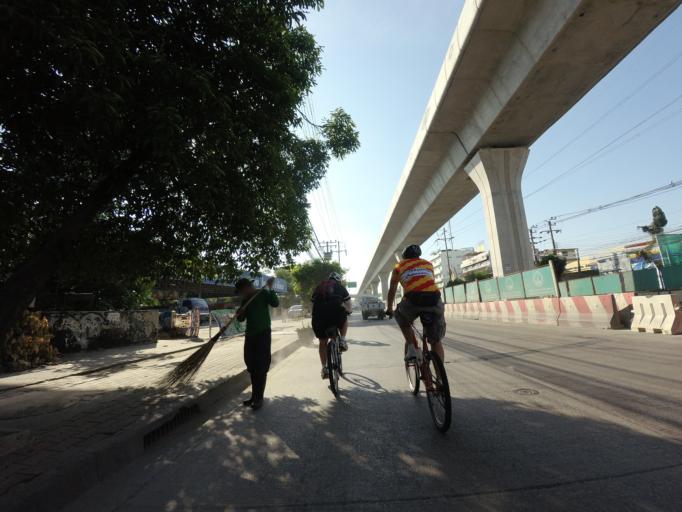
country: TH
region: Samut Prakan
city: Samut Prakan
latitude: 13.6153
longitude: 100.5925
